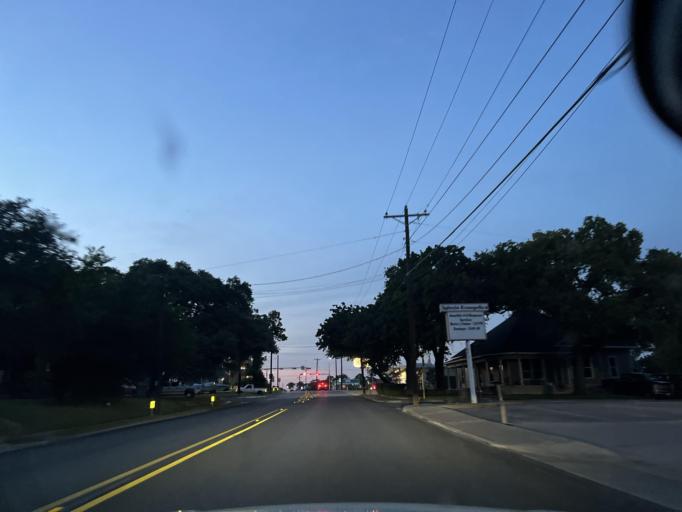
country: US
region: Texas
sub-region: Washington County
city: Brenham
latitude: 30.1750
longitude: -96.4000
